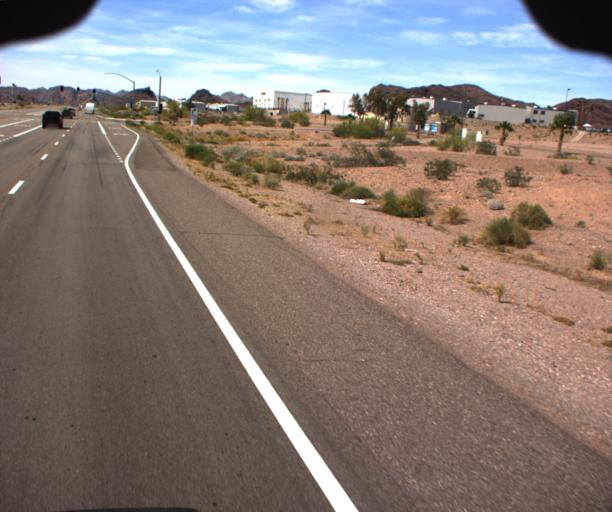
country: US
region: Arizona
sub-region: Mohave County
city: Desert Hills
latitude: 34.5662
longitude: -114.3622
